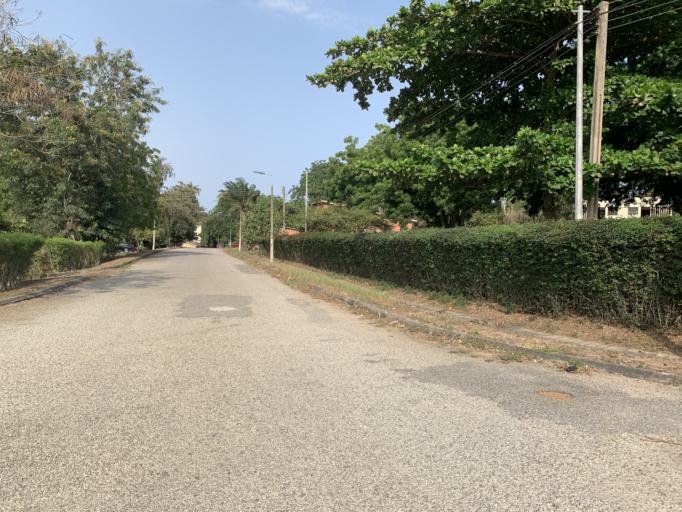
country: GH
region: Central
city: Winneba
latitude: 5.3383
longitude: -0.6291
